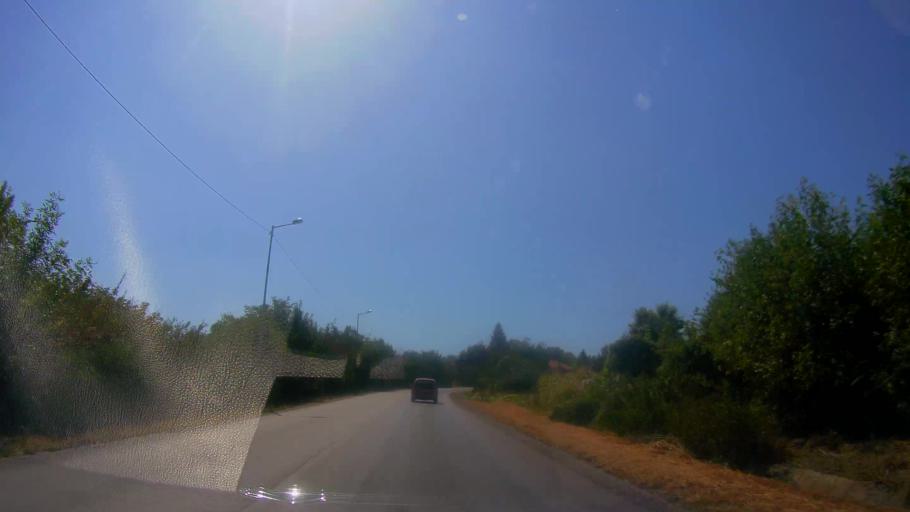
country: BG
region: Veliko Turnovo
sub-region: Obshtina Gorna Oryakhovitsa
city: Purvomaytsi
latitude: 43.1706
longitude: 25.6200
